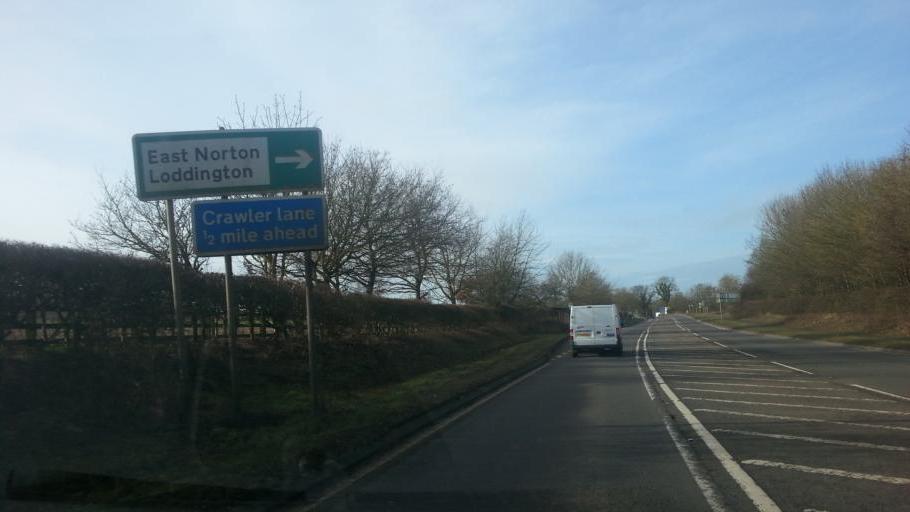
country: GB
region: England
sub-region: District of Rutland
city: Ridlington
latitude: 52.5947
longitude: -0.8462
